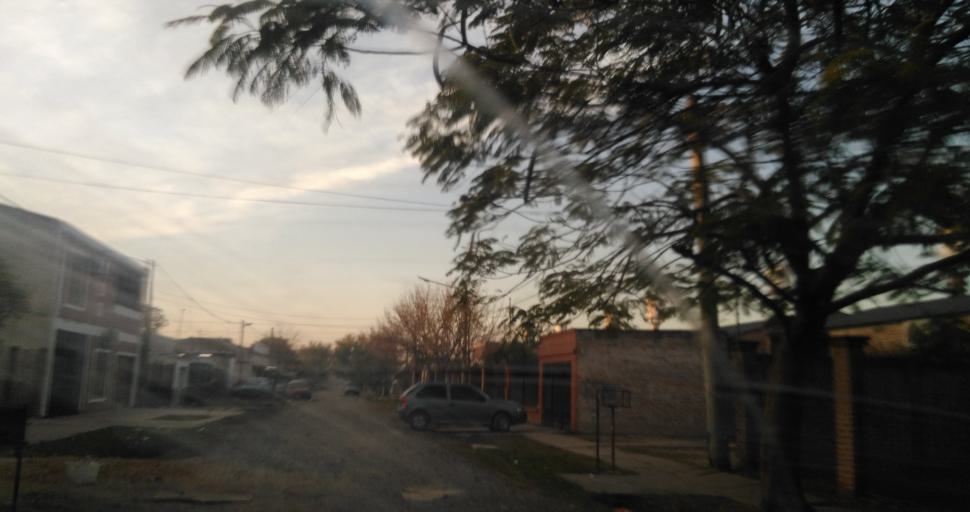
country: AR
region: Chaco
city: Resistencia
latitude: -27.4615
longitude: -59.0119
